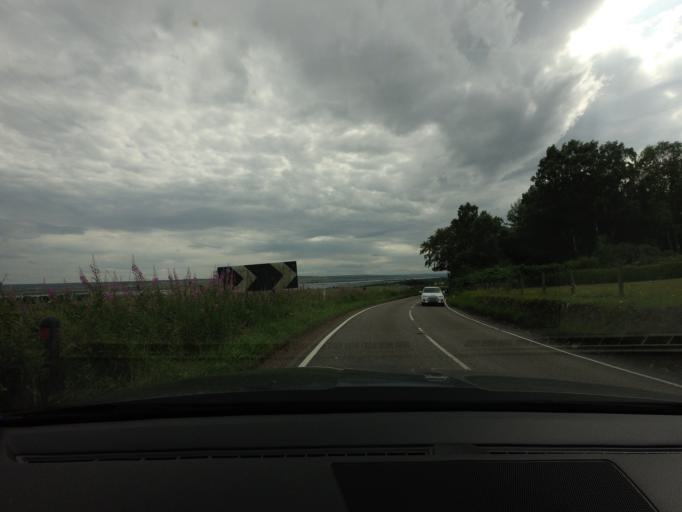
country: GB
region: Scotland
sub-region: Highland
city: Alness
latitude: 57.6974
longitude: -4.2881
